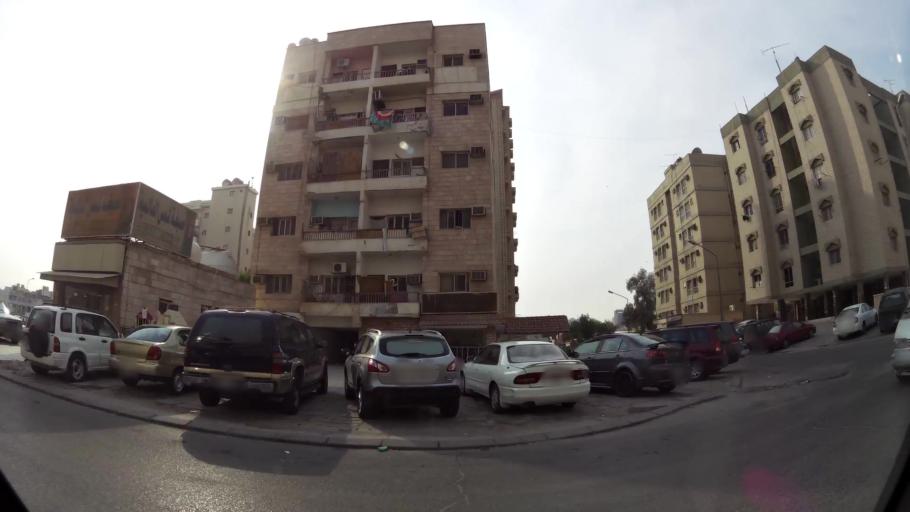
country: KW
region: Al Farwaniyah
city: Al Farwaniyah
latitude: 29.2930
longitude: 47.9743
